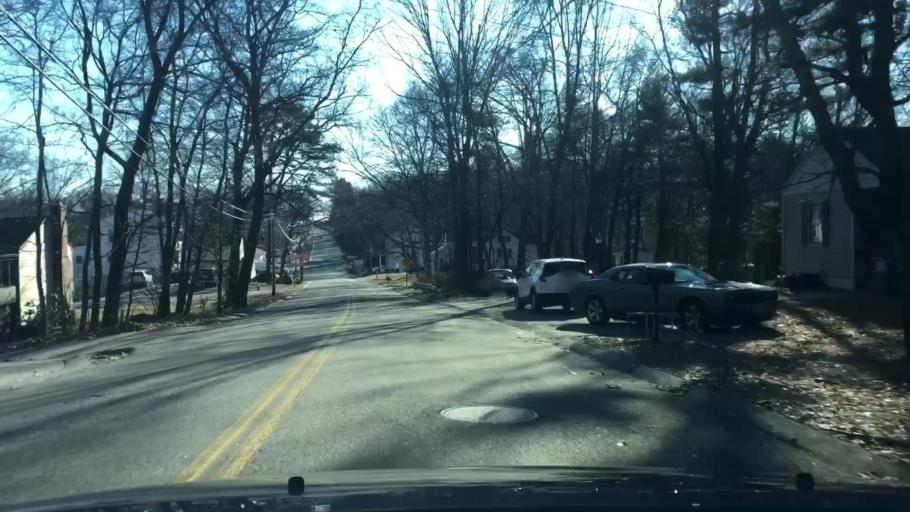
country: US
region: Massachusetts
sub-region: Middlesex County
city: Lowell
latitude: 42.6627
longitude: -71.3412
